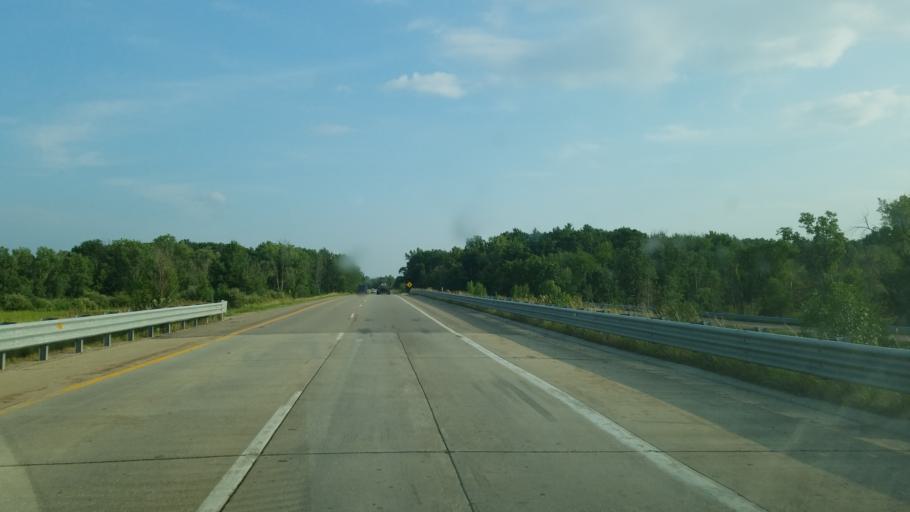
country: US
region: Michigan
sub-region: Gratiot County
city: Ithaca
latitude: 43.3206
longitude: -84.6024
